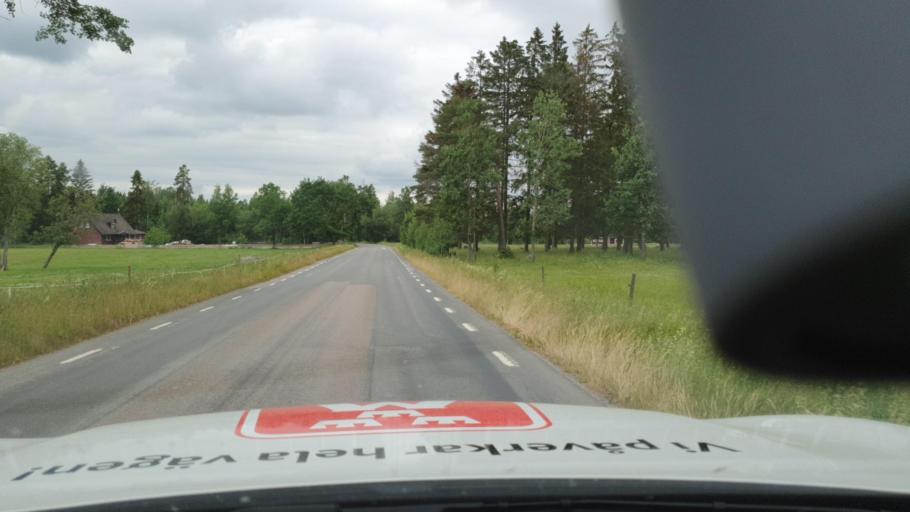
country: SE
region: Vaestra Goetaland
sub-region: Tidaholms Kommun
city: Olofstorp
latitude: 58.3056
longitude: 14.0323
